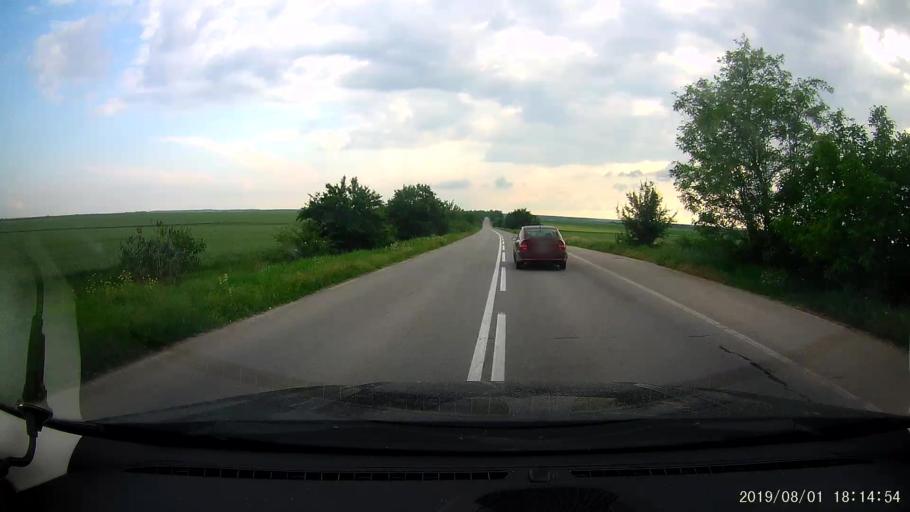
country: BG
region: Silistra
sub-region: Obshtina Dulovo
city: Dulovo
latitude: 43.7618
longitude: 27.1161
